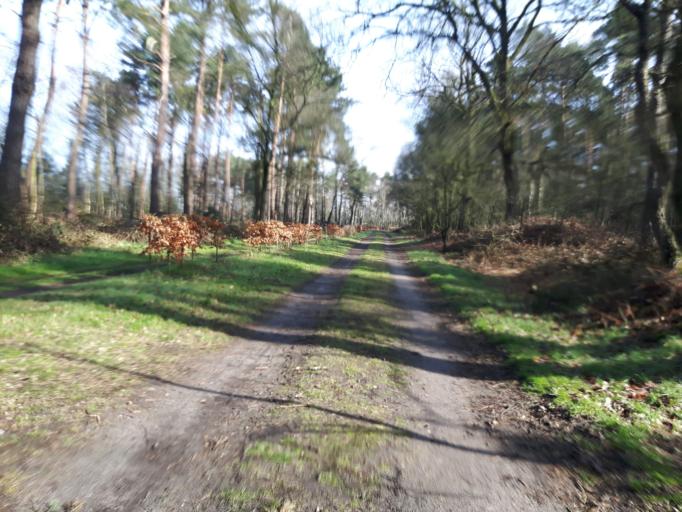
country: DE
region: North Rhine-Westphalia
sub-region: Regierungsbezirk Munster
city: Dulmen
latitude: 51.7920
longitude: 7.2396
